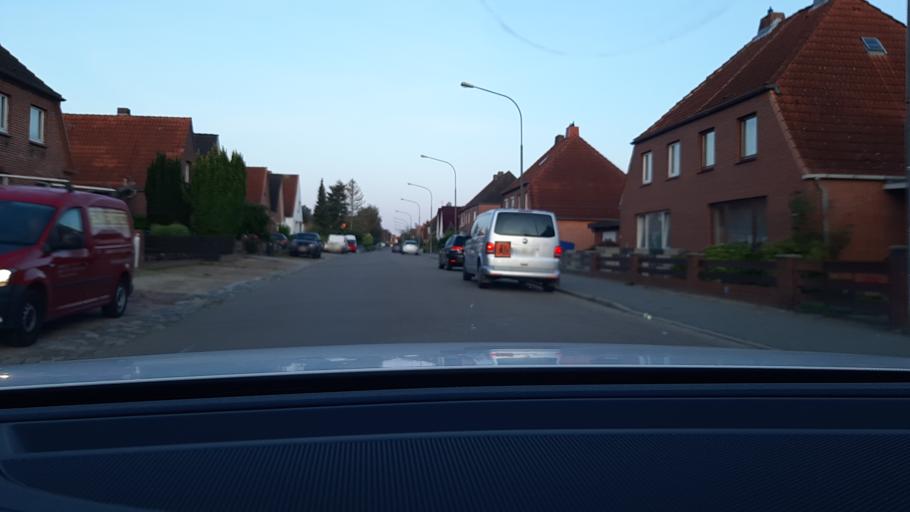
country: DE
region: Schleswig-Holstein
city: Hamberge
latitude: 53.8397
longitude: 10.6287
